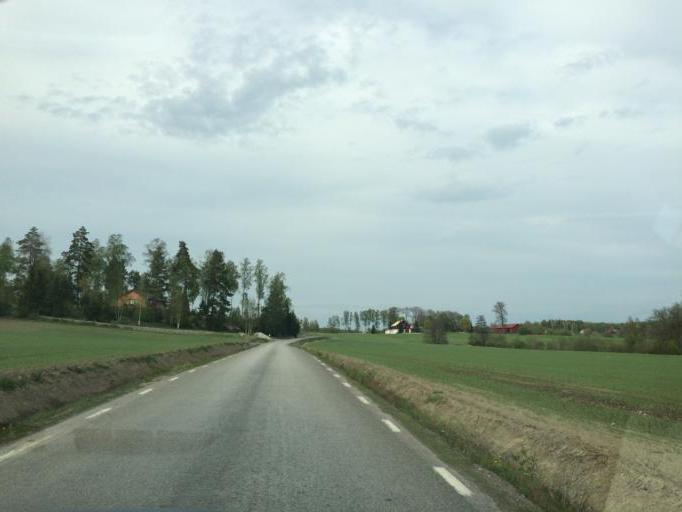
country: SE
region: Vaestmanland
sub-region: Kopings Kommun
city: Koping
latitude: 59.5921
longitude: 15.9941
